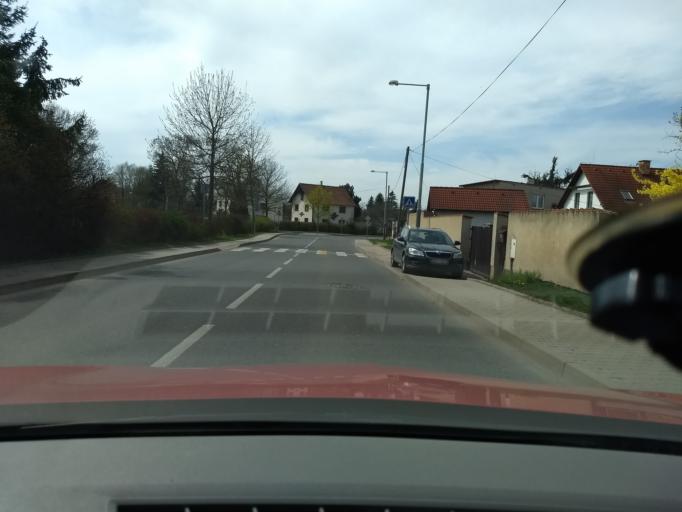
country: CZ
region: Central Bohemia
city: Hostivice
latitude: 50.0656
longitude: 14.2684
